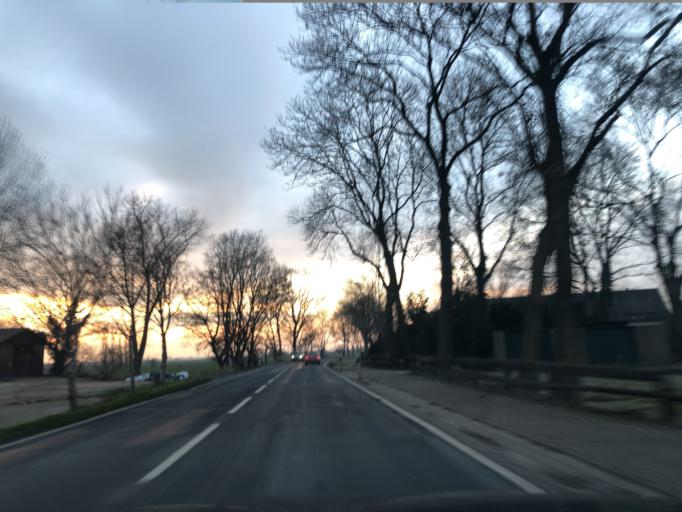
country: DE
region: Lower Saxony
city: Lemwerder
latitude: 53.1364
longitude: 8.6025
